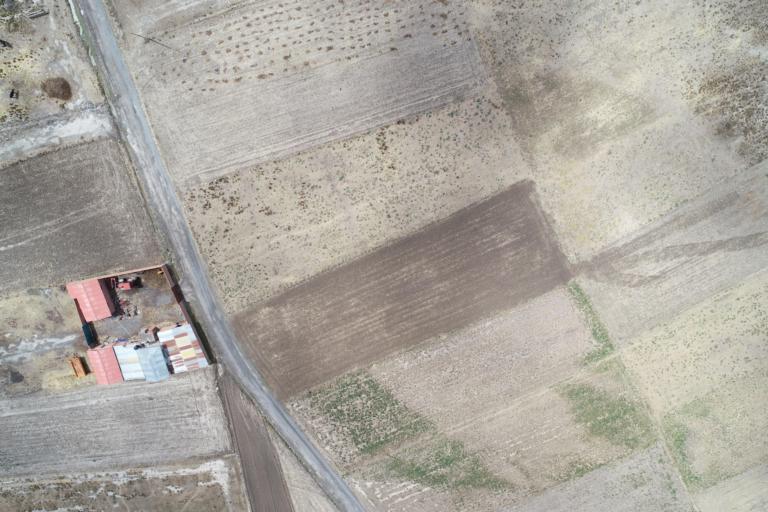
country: BO
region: La Paz
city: Achacachi
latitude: -16.0309
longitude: -68.6906
